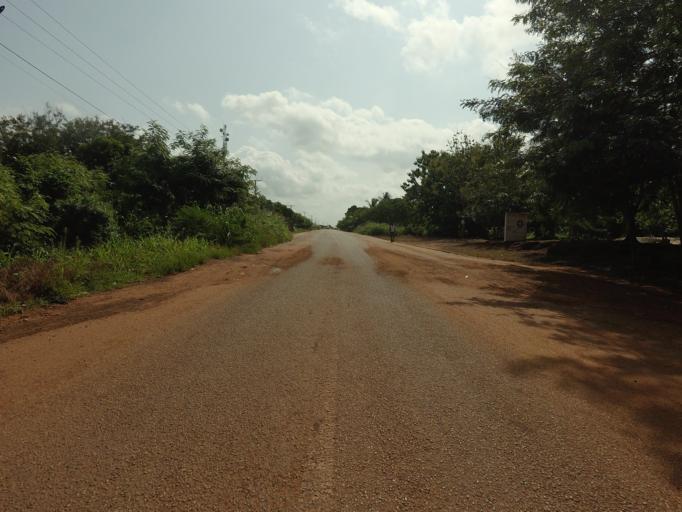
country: TG
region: Maritime
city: Tsevie
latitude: 6.3611
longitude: 0.8639
